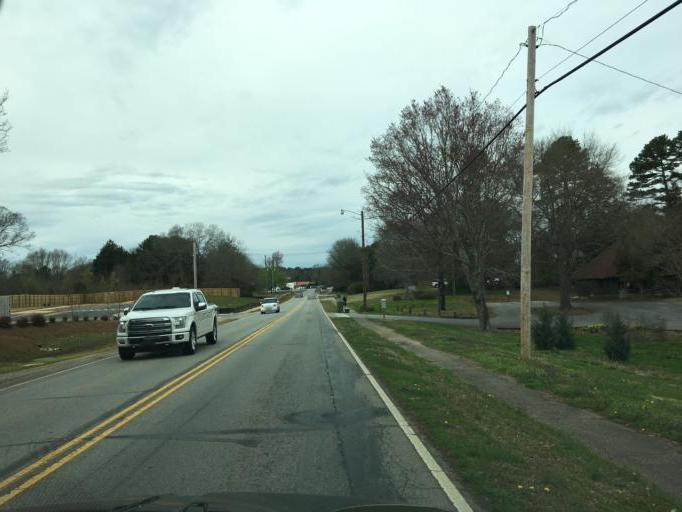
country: US
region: South Carolina
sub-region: Anderson County
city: Pendleton
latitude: 34.6713
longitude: -82.8076
